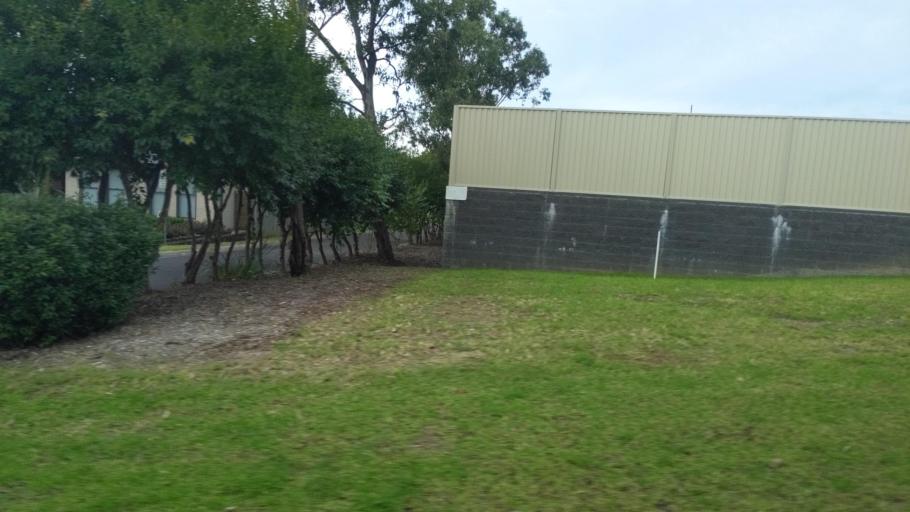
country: AU
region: New South Wales
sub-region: Blacktown
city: Quakers Hill
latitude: -33.7305
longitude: 150.8660
